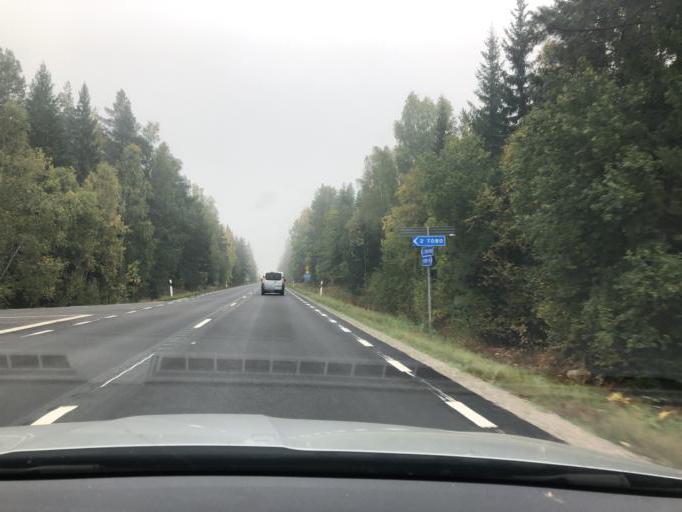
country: SE
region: Uppsala
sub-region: Tierps Kommun
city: Orbyhus
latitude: 60.2453
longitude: 17.6539
